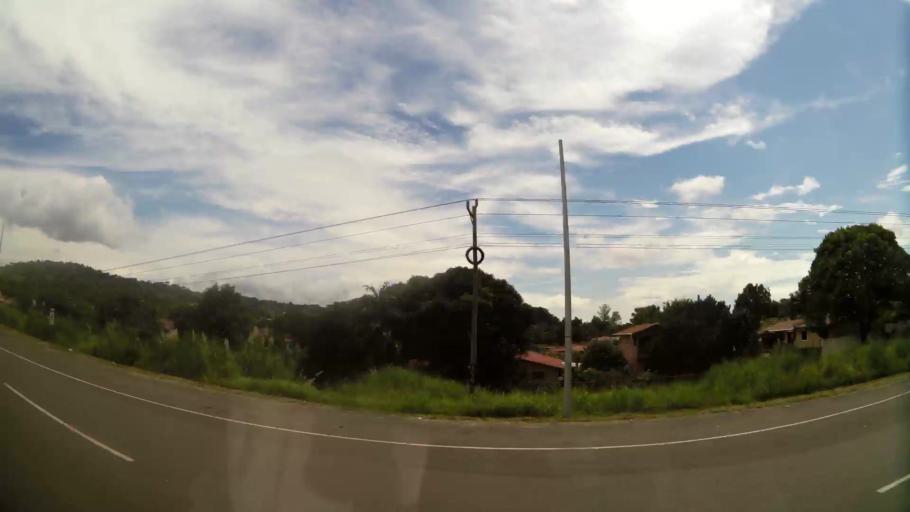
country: PA
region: Panama
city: Vista Alegre
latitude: 8.9254
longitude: -79.6964
